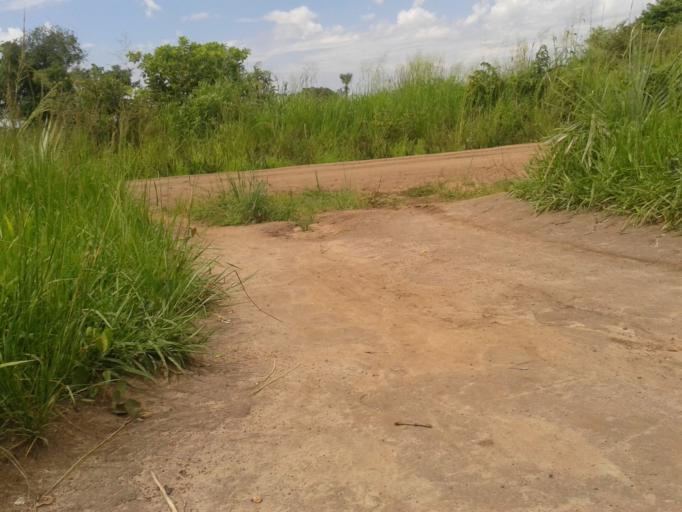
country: UG
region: Northern Region
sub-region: Gulu District
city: Gulu
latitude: 2.8280
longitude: 32.2539
